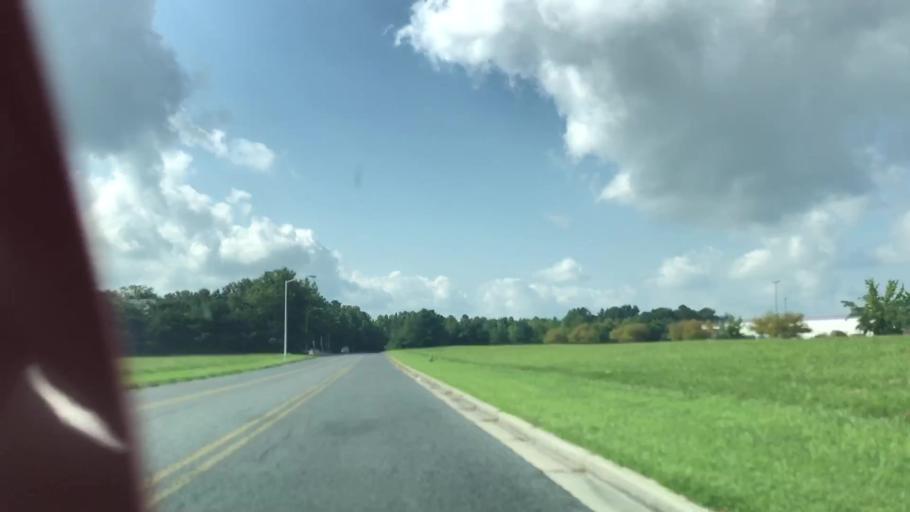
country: US
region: Maryland
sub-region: Wicomico County
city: Salisbury
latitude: 38.3995
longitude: -75.5627
